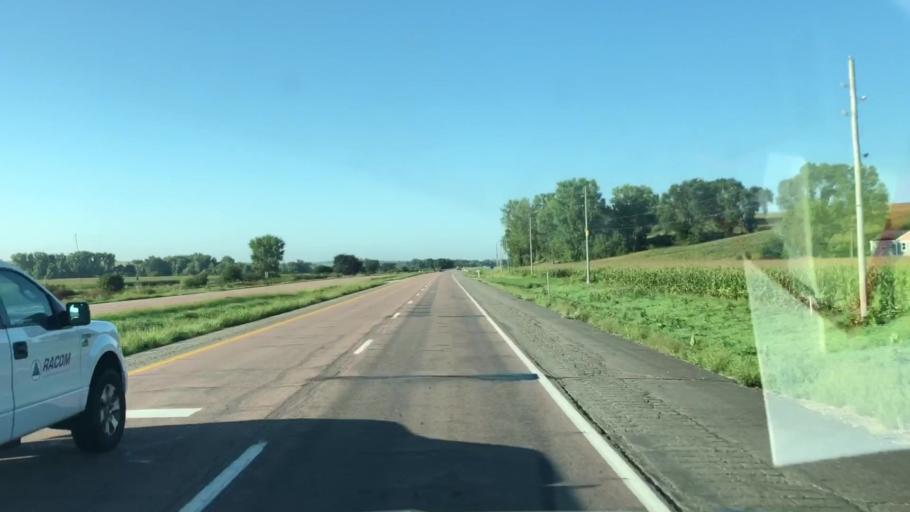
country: US
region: Iowa
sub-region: Woodbury County
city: Sioux City
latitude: 42.5884
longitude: -96.3081
